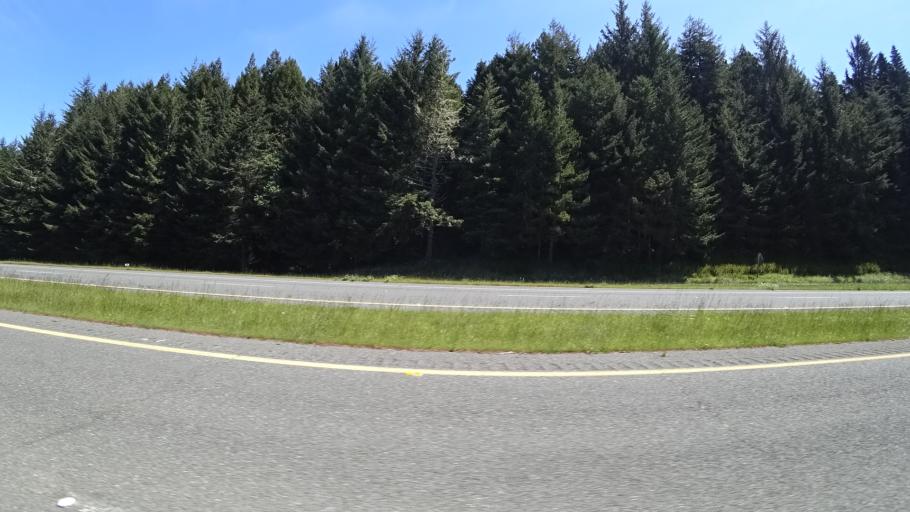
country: US
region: California
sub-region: Humboldt County
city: Westhaven-Moonstone
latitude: 41.0978
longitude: -124.1531
